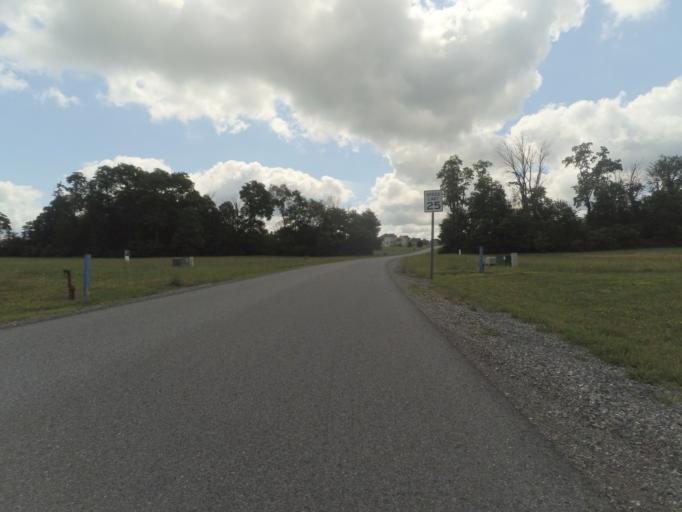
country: US
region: Pennsylvania
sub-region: Centre County
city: Stormstown
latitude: 40.8029
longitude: -77.9983
